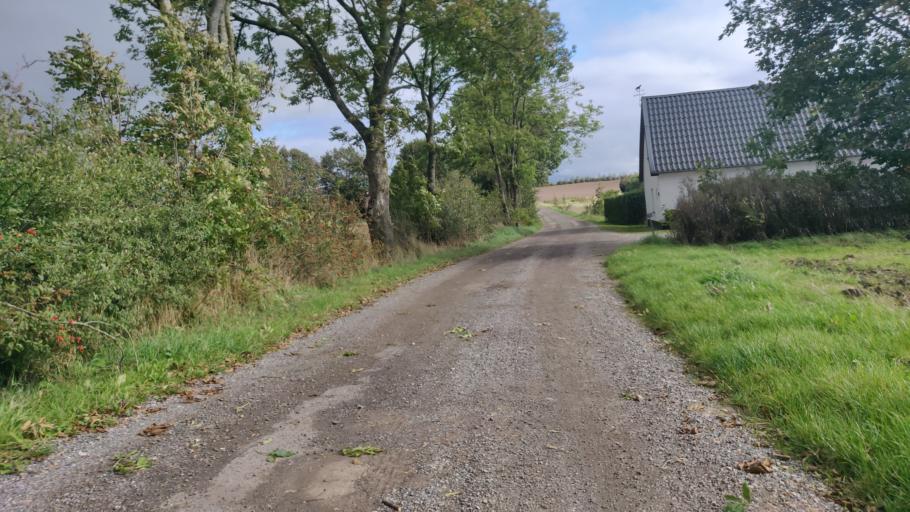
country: DK
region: South Denmark
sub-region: Kolding Kommune
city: Lunderskov
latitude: 55.5369
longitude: 9.3672
